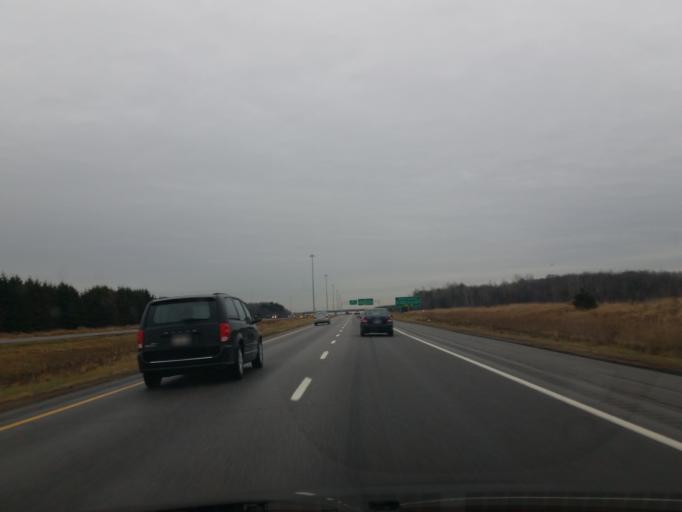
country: CA
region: Quebec
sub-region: Capitale-Nationale
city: Saint-Augustin-de-Desmaures
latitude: 46.7537
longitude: -71.4870
